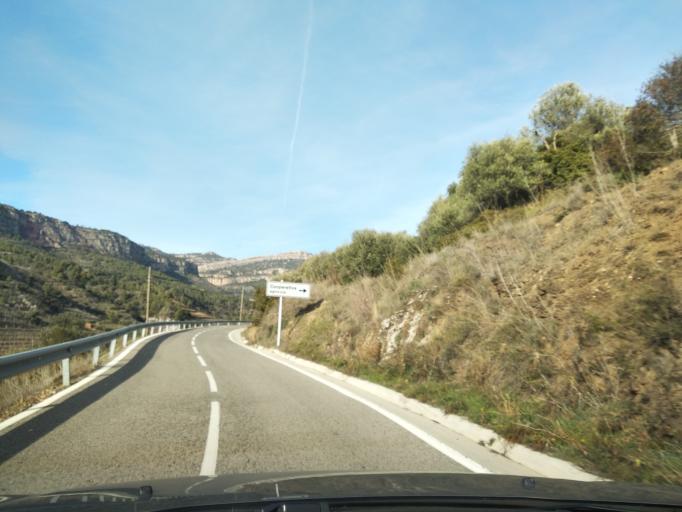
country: ES
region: Catalonia
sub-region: Provincia de Tarragona
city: Margalef
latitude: 41.2266
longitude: 0.7782
